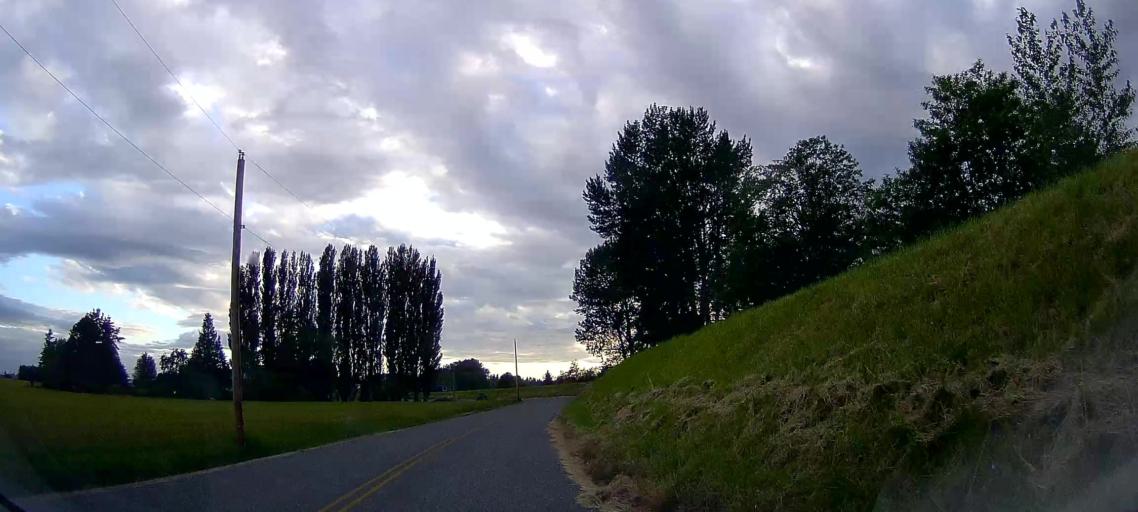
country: US
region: Washington
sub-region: Skagit County
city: Mount Vernon
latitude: 48.3678
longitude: -122.4018
